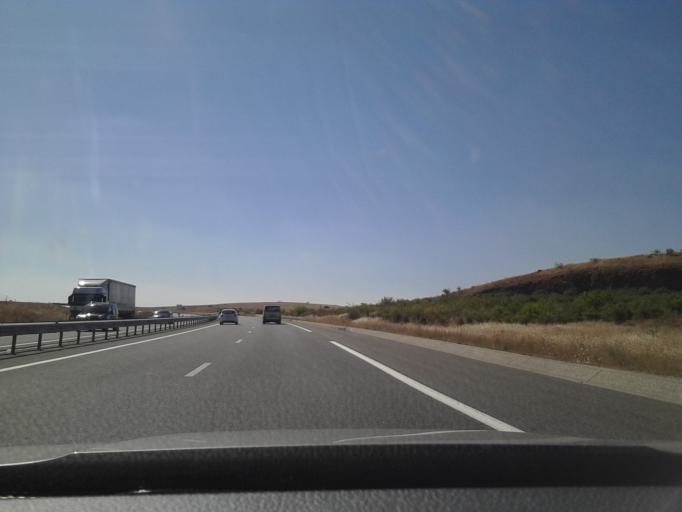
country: FR
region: Midi-Pyrenees
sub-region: Departement de l'Aveyron
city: Creissels
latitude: 44.0297
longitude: 3.0691
